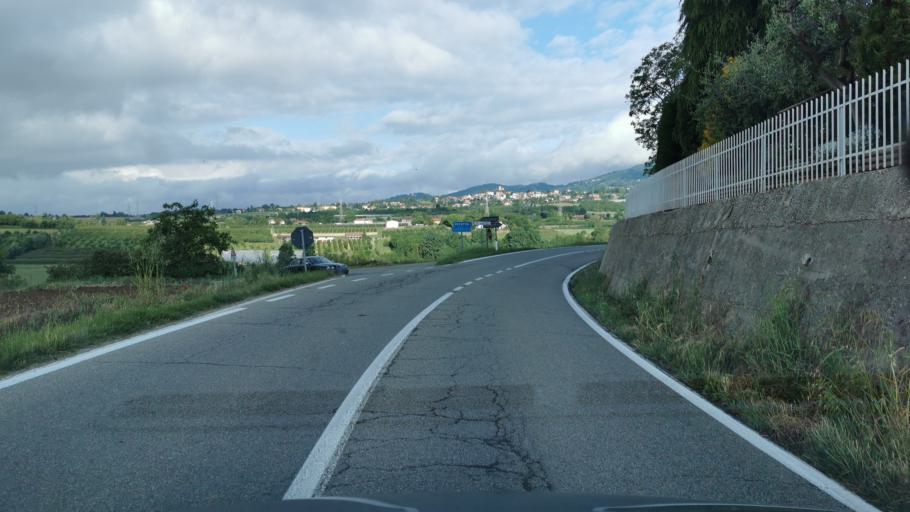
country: IT
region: Piedmont
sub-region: Provincia di Torino
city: Pino Torinese
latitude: 45.0139
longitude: 7.7795
